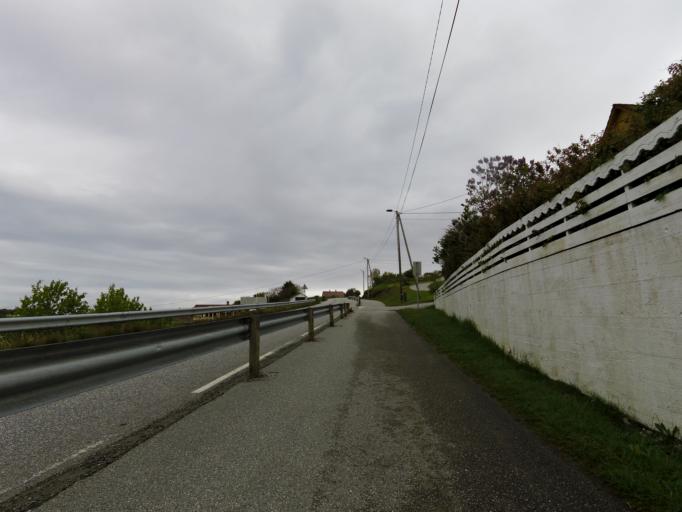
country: NO
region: Hordaland
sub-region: Sveio
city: Sveio
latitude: 59.6016
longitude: 5.2138
